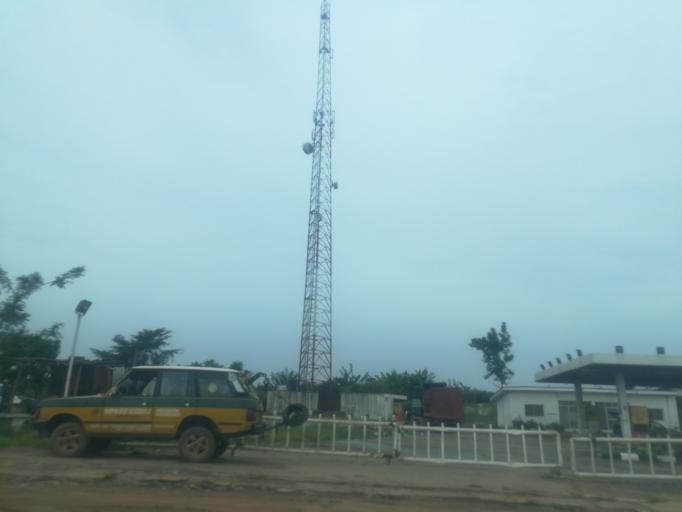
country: NG
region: Oyo
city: Egbeda
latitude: 7.3824
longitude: 4.0181
